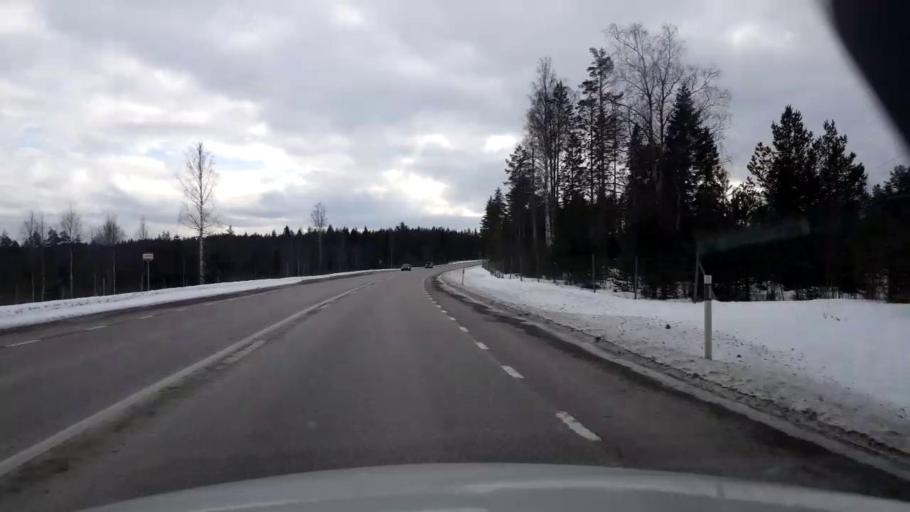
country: SE
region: Gaevleborg
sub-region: Nordanstigs Kommun
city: Bergsjoe
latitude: 62.0002
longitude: 17.2405
